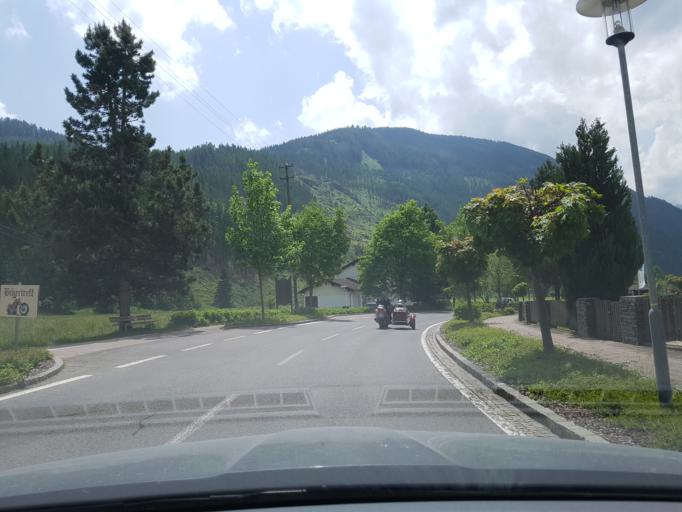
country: AT
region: Carinthia
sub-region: Politischer Bezirk Feldkirchen
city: Gnesau
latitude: 46.8540
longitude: 13.8939
